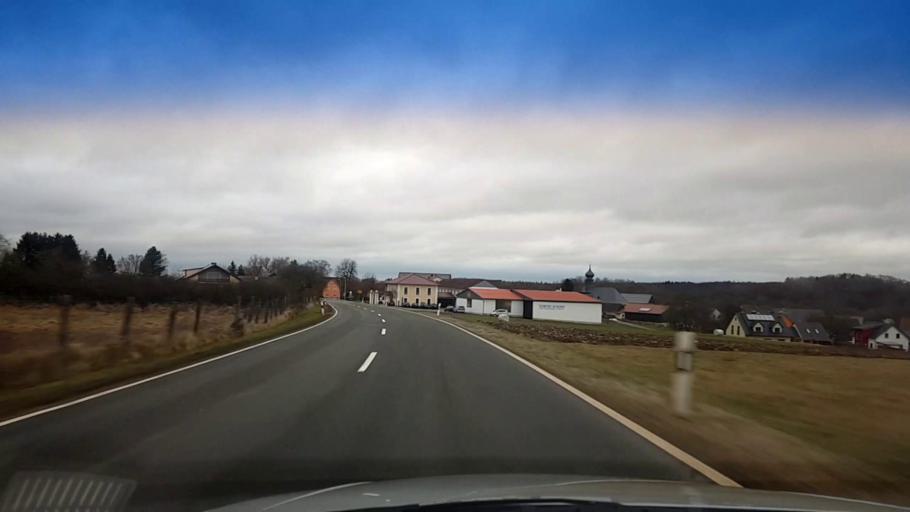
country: DE
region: Bavaria
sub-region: Upper Franconia
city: Wattendorf
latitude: 50.0427
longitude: 11.0959
